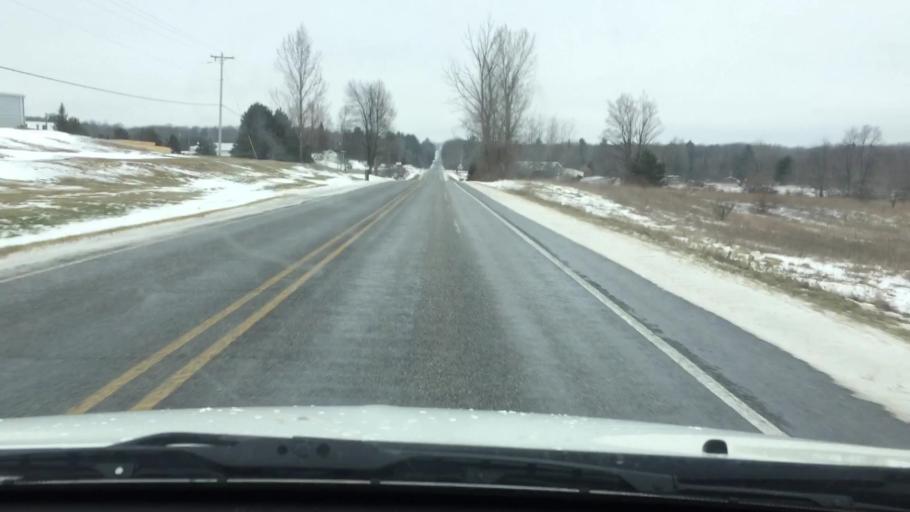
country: US
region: Michigan
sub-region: Wexford County
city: Cadillac
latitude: 44.0648
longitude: -85.4440
